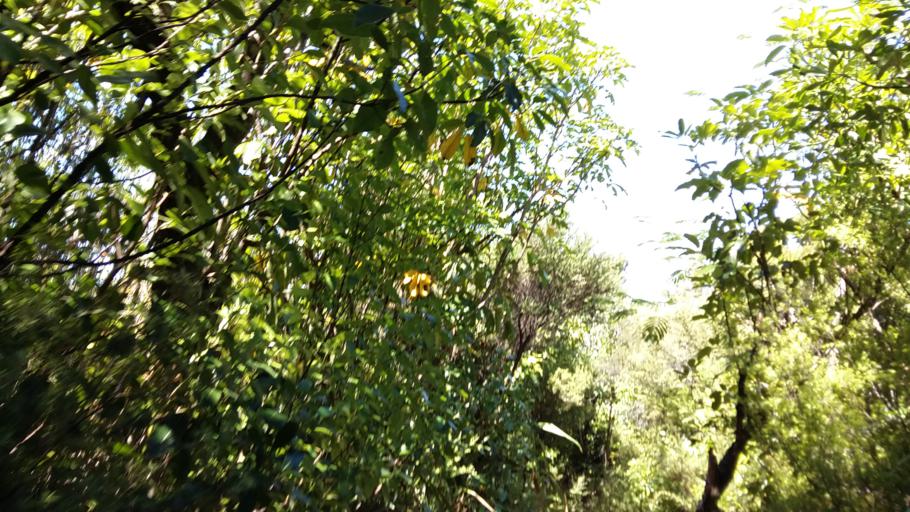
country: NZ
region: Bay of Plenty
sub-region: Whakatane District
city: Whakatane
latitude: -37.9446
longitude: 177.0194
